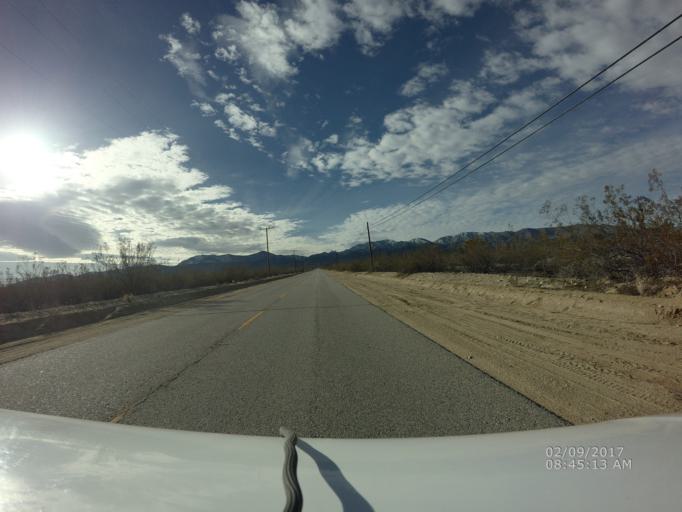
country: US
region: California
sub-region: Los Angeles County
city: Lake Los Angeles
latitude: 34.5005
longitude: -117.8354
